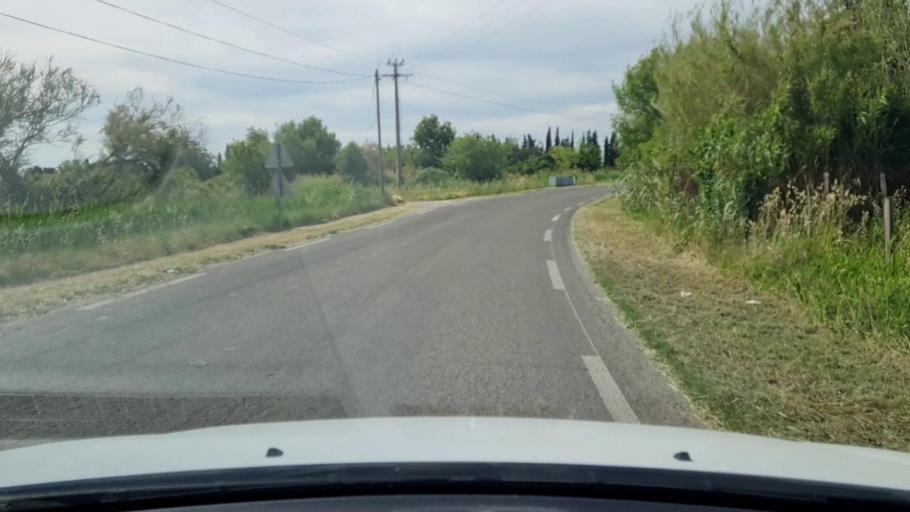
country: FR
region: Languedoc-Roussillon
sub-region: Departement du Gard
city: Aigues-Mortes
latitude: 43.6067
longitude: 4.2142
